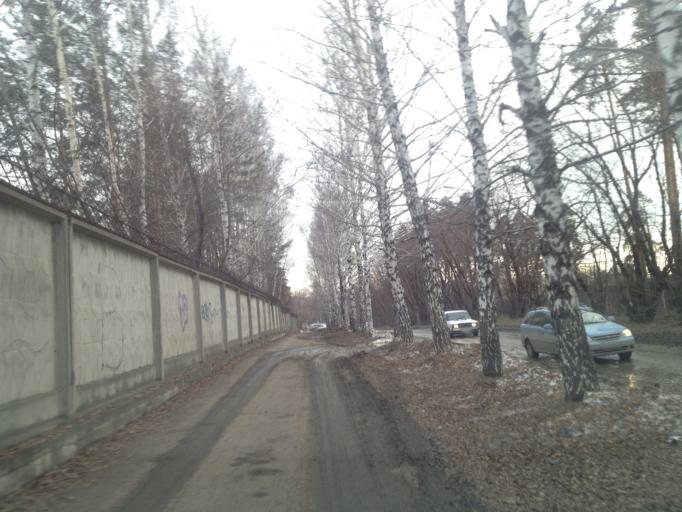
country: RU
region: Sverdlovsk
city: Shuvakish
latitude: 56.8748
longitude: 60.5367
